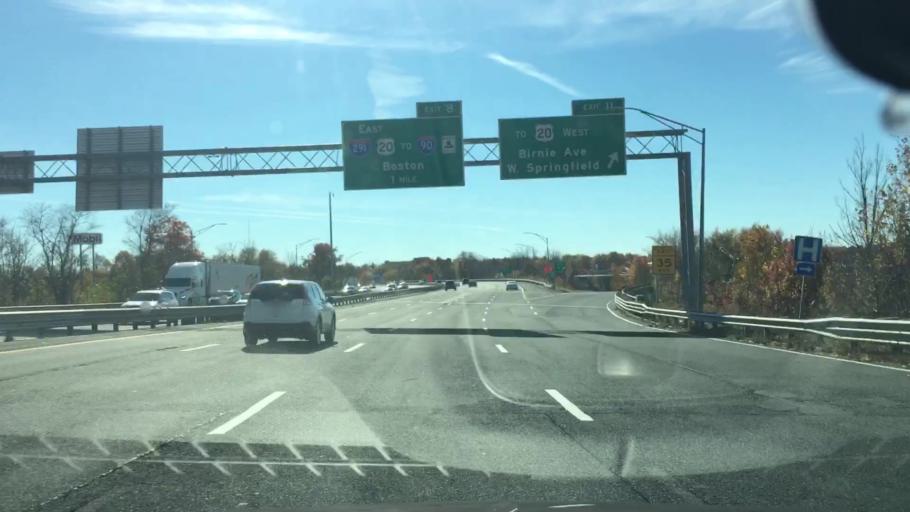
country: US
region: Massachusetts
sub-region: Hampden County
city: West Springfield
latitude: 42.1224
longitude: -72.6086
